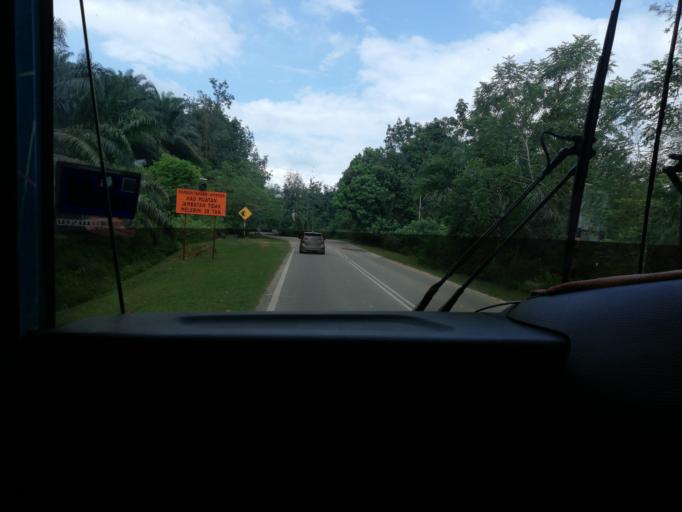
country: MY
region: Kedah
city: Kulim
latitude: 5.3346
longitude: 100.5879
